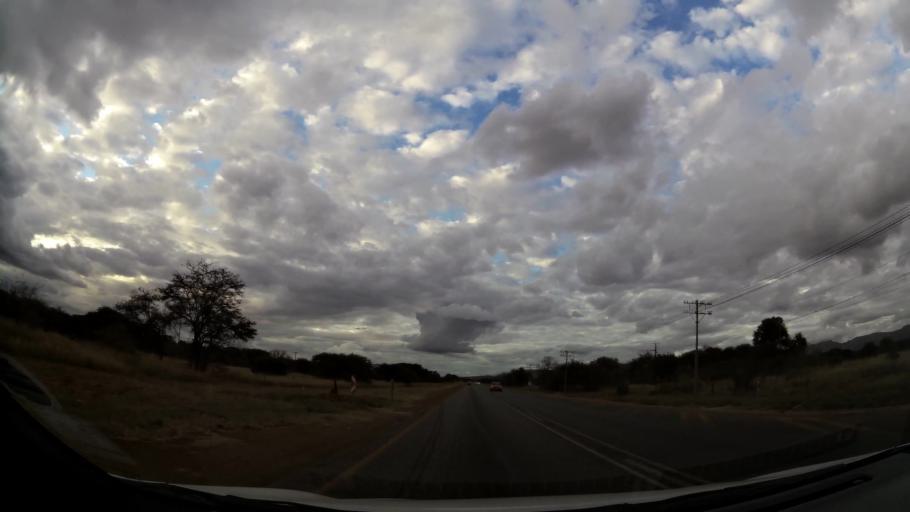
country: ZA
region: Limpopo
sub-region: Waterberg District Municipality
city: Mokopane
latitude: -24.2268
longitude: 29.0012
